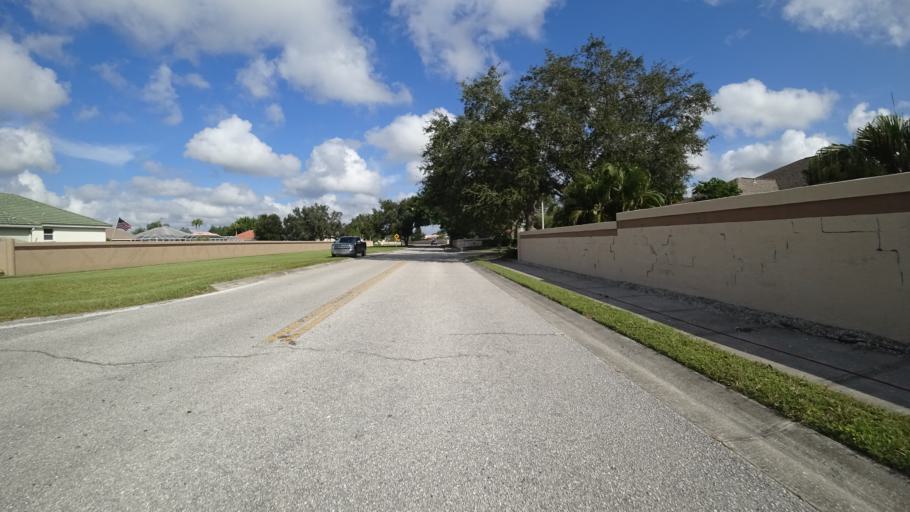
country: US
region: Florida
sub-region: Sarasota County
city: North Sarasota
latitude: 27.4098
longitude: -82.5135
